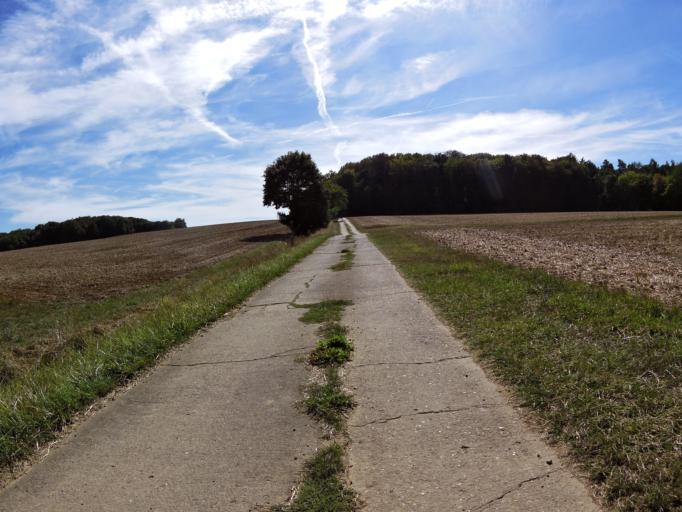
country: DE
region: Bavaria
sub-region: Regierungsbezirk Unterfranken
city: Eisingen
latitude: 49.7739
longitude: 9.8361
